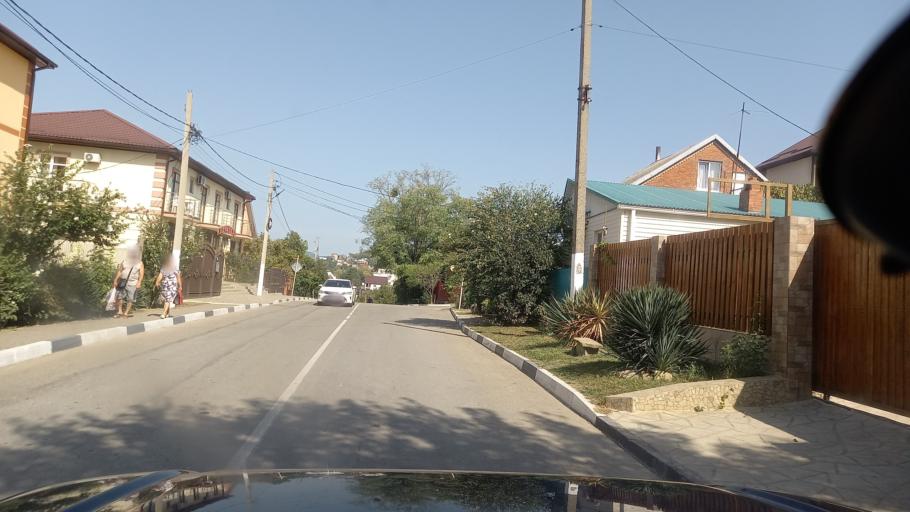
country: RU
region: Krasnodarskiy
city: Arkhipo-Osipovka
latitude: 44.3659
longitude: 38.5312
